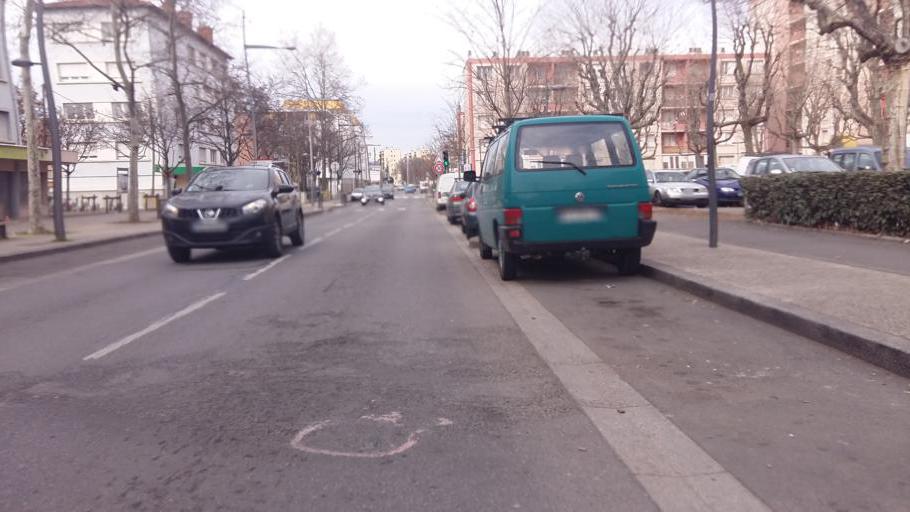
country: FR
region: Rhone-Alpes
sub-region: Departement du Rhone
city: Villeurbanne
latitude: 45.7790
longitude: 4.8919
